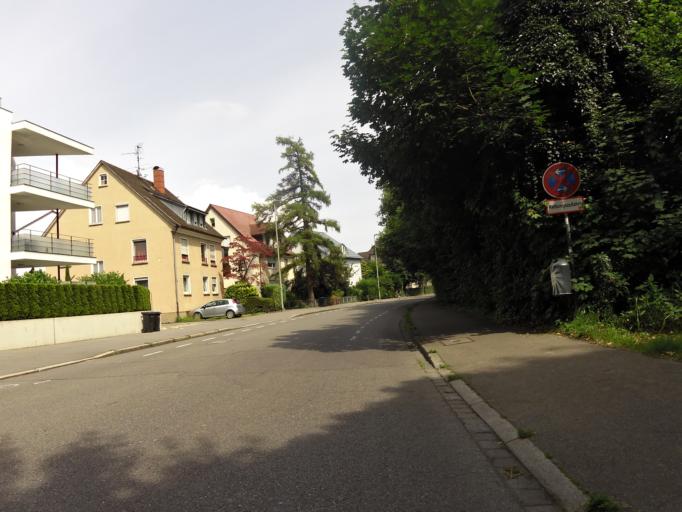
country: DE
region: Baden-Wuerttemberg
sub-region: Tuebingen Region
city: Friedrichshafen
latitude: 47.6525
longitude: 9.4904
